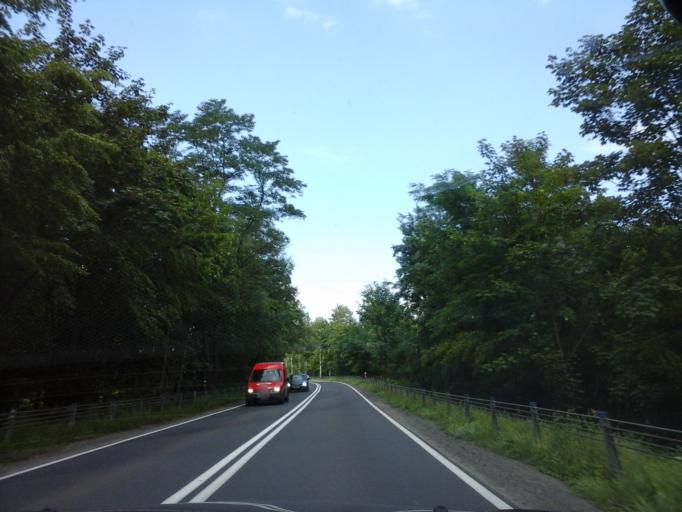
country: PL
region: Lesser Poland Voivodeship
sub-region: Powiat suski
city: Zembrzyce
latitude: 49.7717
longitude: 19.5924
